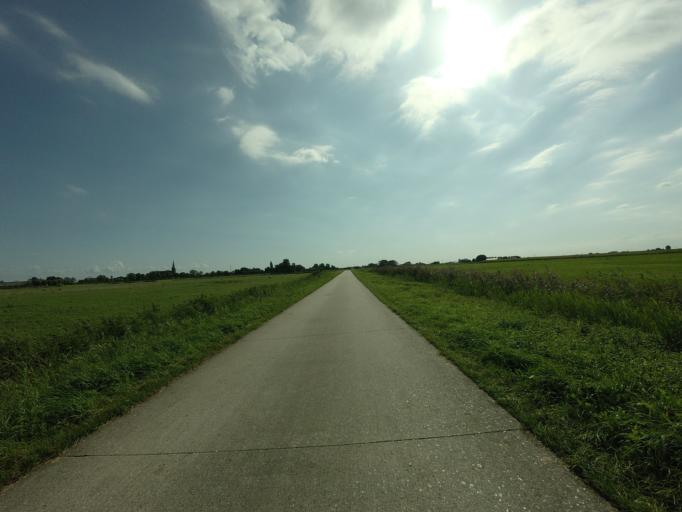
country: NL
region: Friesland
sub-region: Gemeente Littenseradiel
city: Makkum
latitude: 53.0818
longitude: 5.6318
